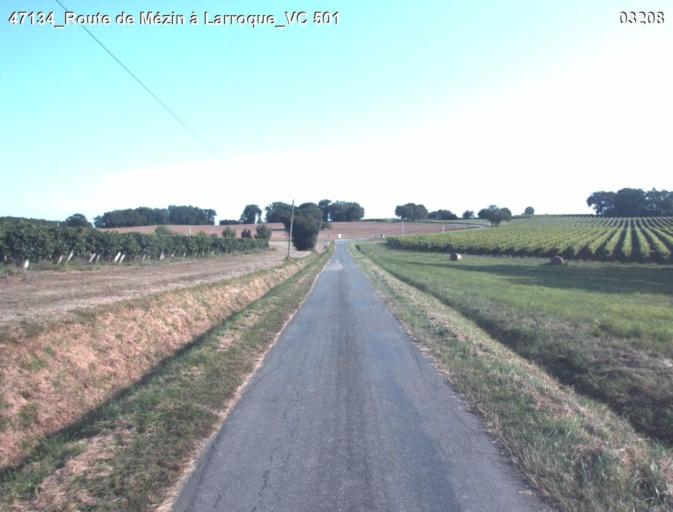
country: FR
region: Aquitaine
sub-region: Departement du Lot-et-Garonne
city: Mezin
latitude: 44.0237
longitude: 0.2704
